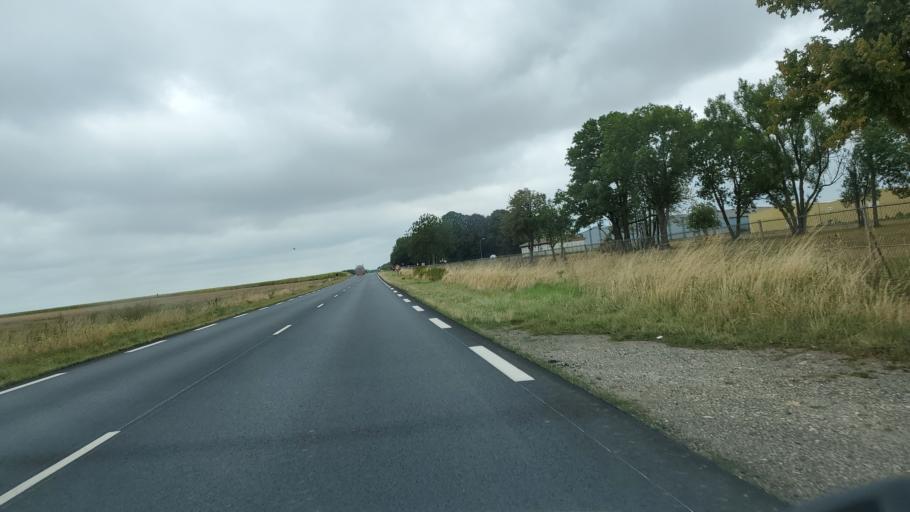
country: FR
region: Ile-de-France
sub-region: Departement de Seine-et-Marne
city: Pommeuse
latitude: 48.8324
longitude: 3.0074
